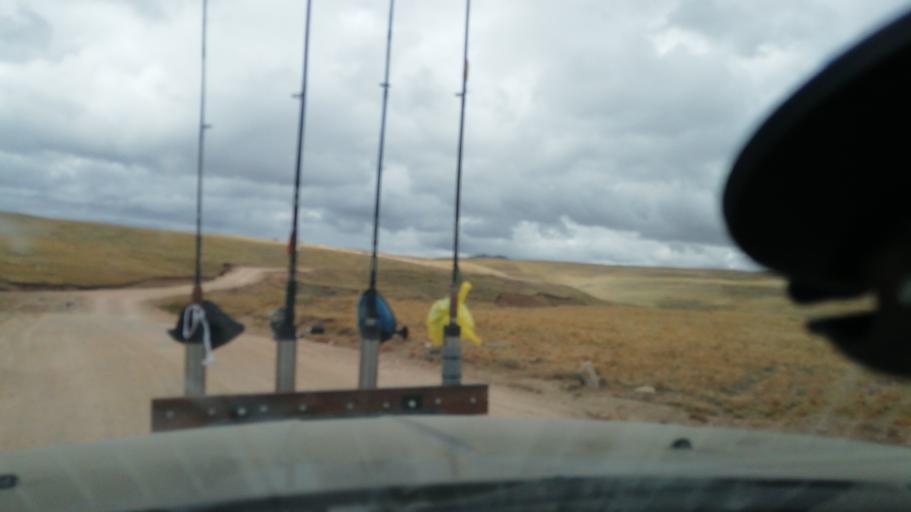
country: PE
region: Huancavelica
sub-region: Provincia de Huancavelica
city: Acobambilla
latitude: -12.5533
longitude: -75.5444
